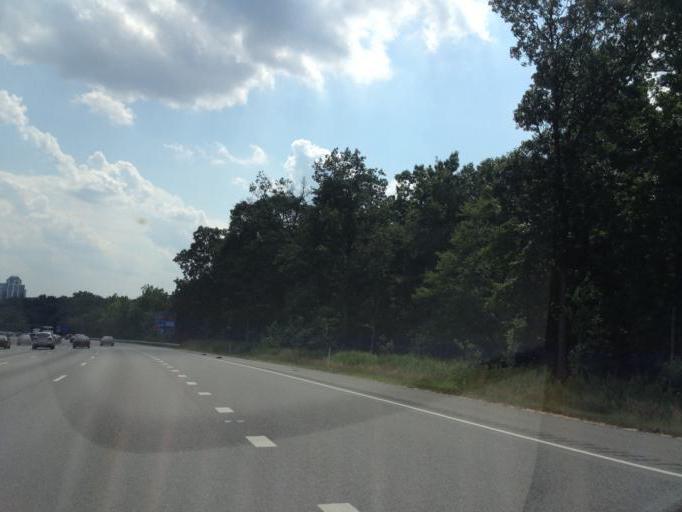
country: US
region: Maryland
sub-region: Prince George's County
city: Calverton
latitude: 39.0601
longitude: -76.9239
